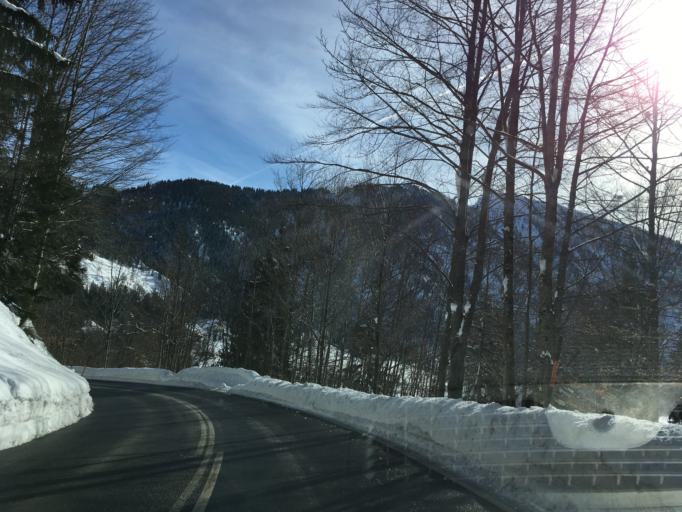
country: DE
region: Bavaria
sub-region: Upper Bavaria
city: Bayrischzell
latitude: 47.6788
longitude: 12.0145
